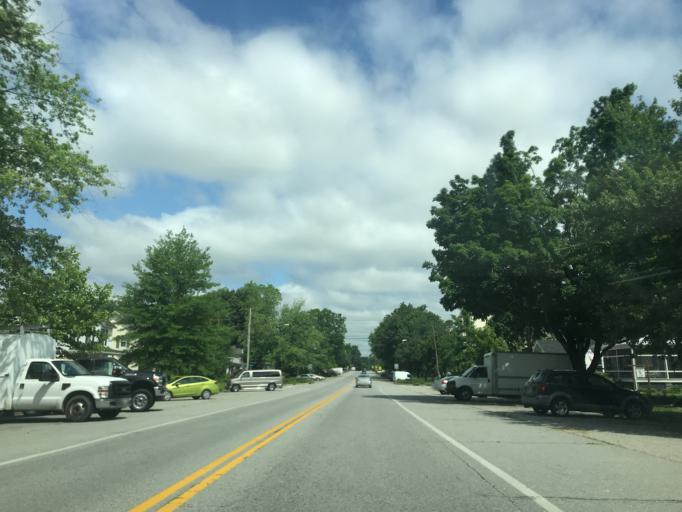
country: US
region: Maryland
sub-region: Caroline County
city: Ridgely
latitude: 38.9441
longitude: -75.8821
